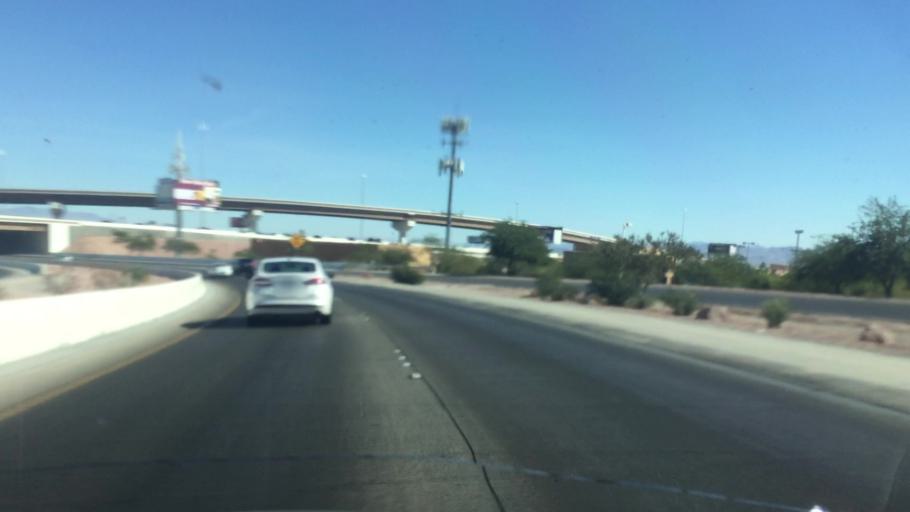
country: US
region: Nevada
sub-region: Clark County
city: Paradise
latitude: 36.0612
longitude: -115.1518
